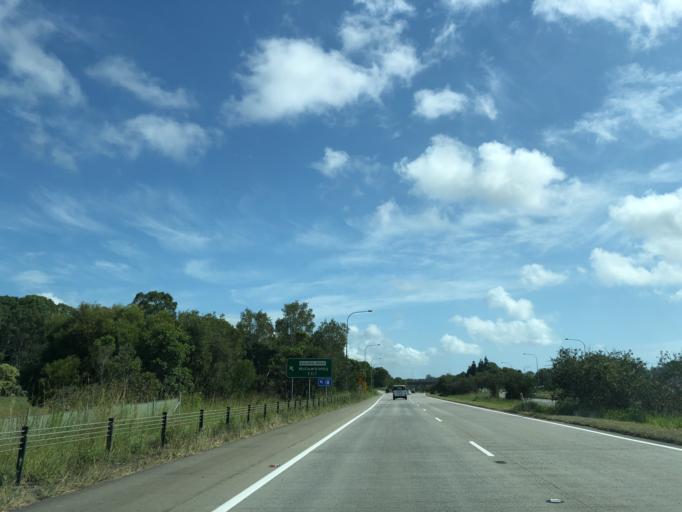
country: AU
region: New South Wales
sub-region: Byron Shire
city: Brunswick Heads
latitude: -28.5885
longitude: 153.5445
